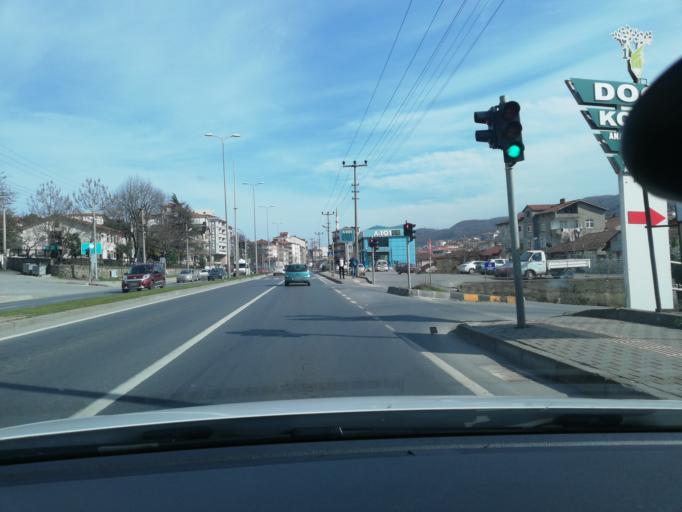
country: TR
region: Zonguldak
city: Eregli
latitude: 41.2698
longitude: 31.4477
